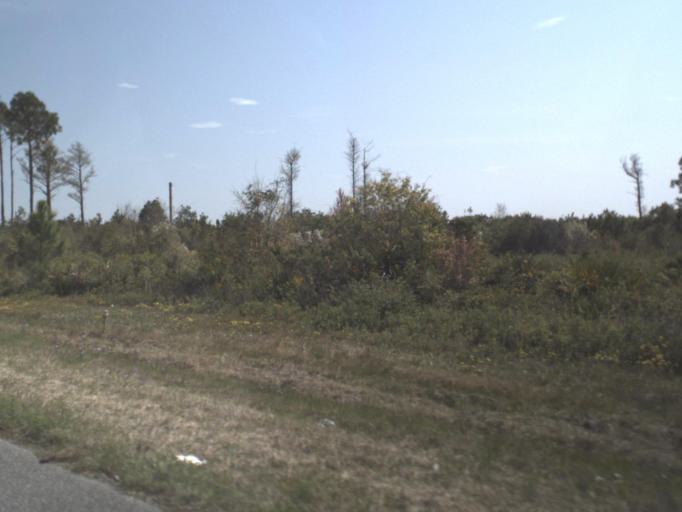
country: US
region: Florida
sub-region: Franklin County
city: Apalachicola
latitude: 29.7243
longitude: -85.0777
